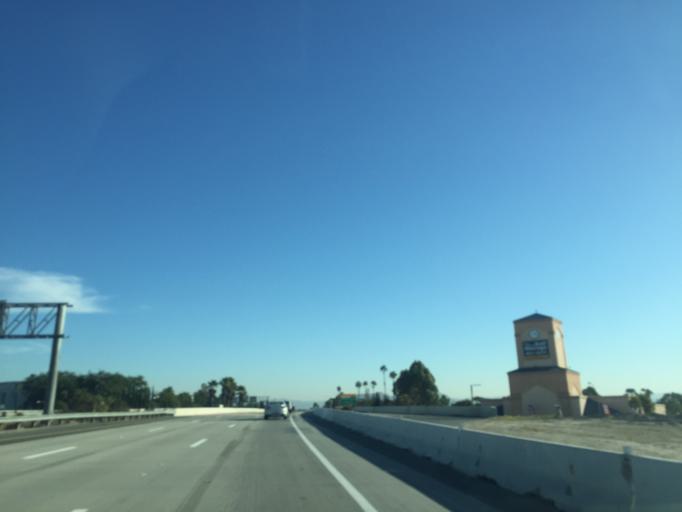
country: MX
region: Baja California
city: Tijuana
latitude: 32.5611
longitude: -116.9452
